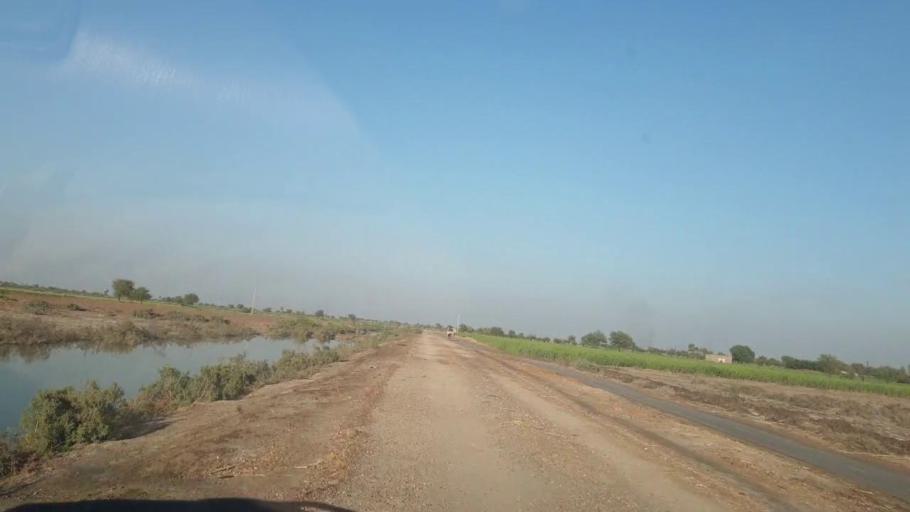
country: PK
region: Sindh
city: Mirpur Khas
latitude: 25.4500
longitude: 69.1097
